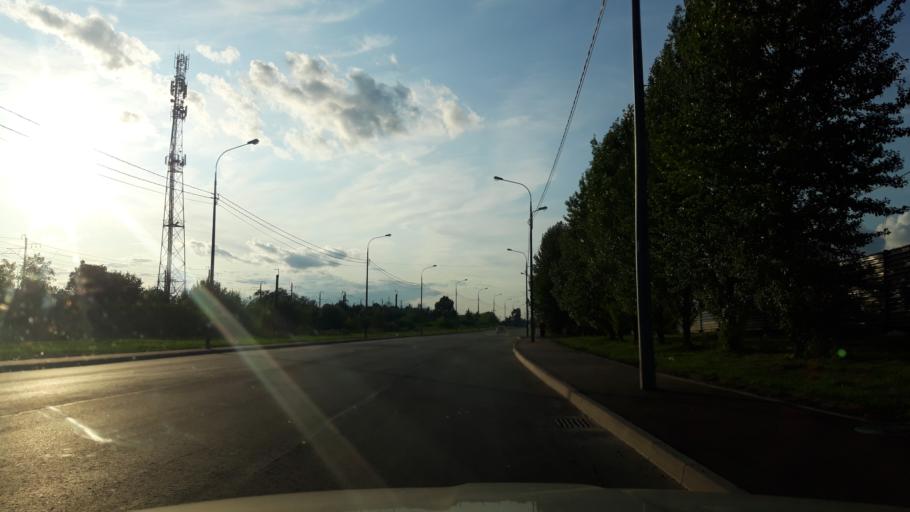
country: RU
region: Moskovskaya
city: Alabushevo
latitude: 56.0044
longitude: 37.1469
